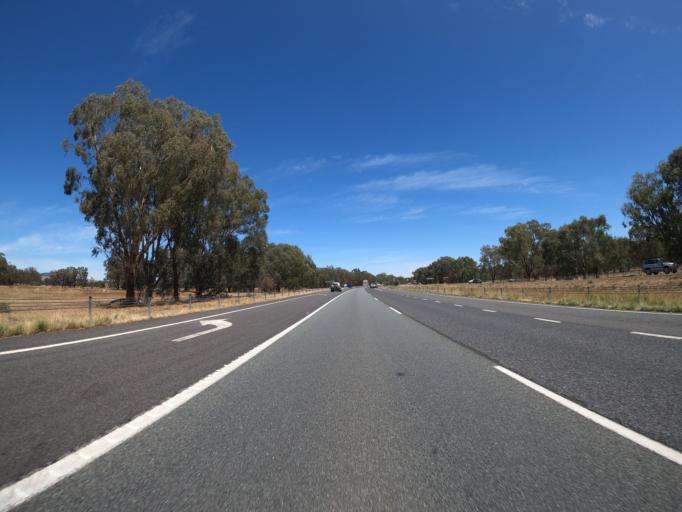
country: AU
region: Victoria
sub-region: Benalla
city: Benalla
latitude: -36.6013
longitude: 145.8684
